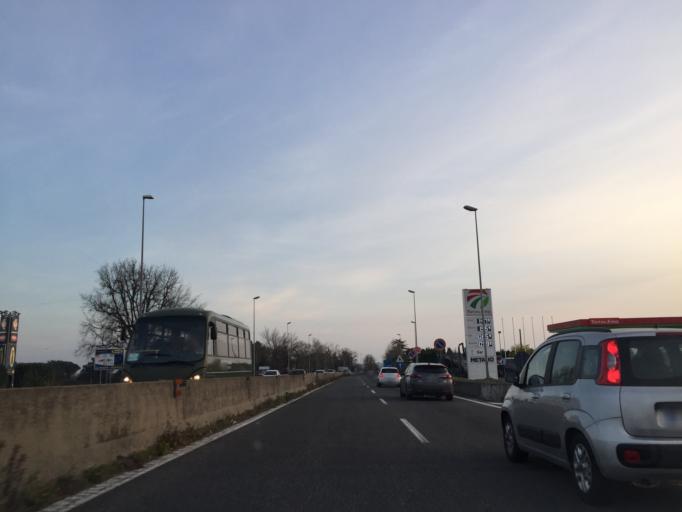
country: IT
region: Latium
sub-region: Citta metropolitana di Roma Capitale
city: Le Rughe
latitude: 42.0626
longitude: 12.3729
